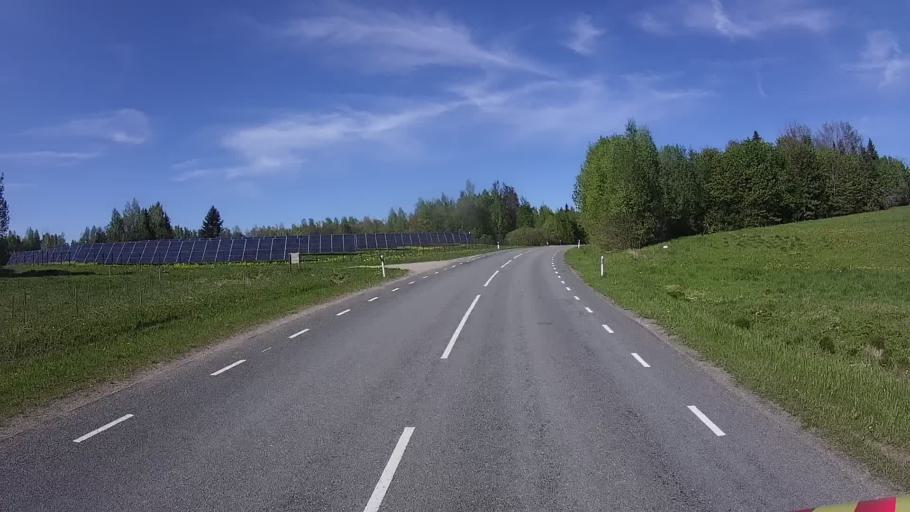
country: EE
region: Vorumaa
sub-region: Antsla vald
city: Vana-Antsla
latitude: 57.9787
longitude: 26.4663
